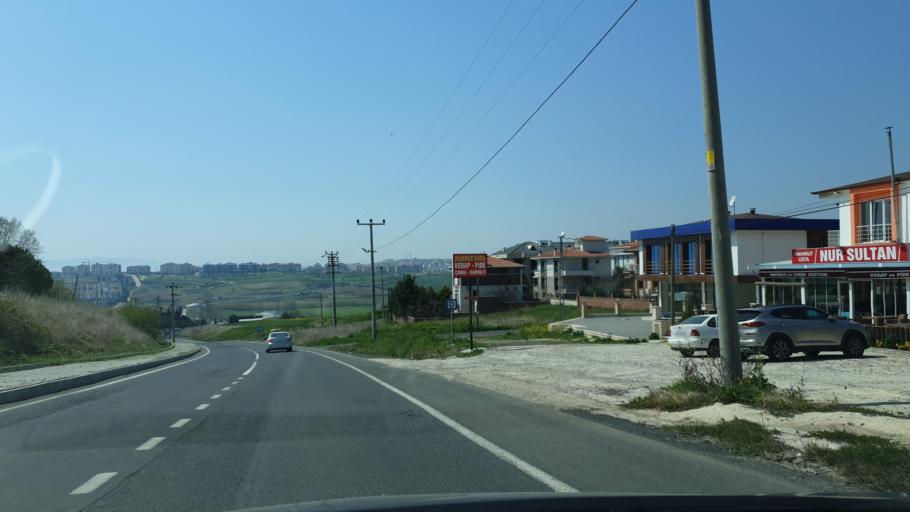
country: TR
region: Tekirdag
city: Tekirdag
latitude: 40.9973
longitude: 27.5837
